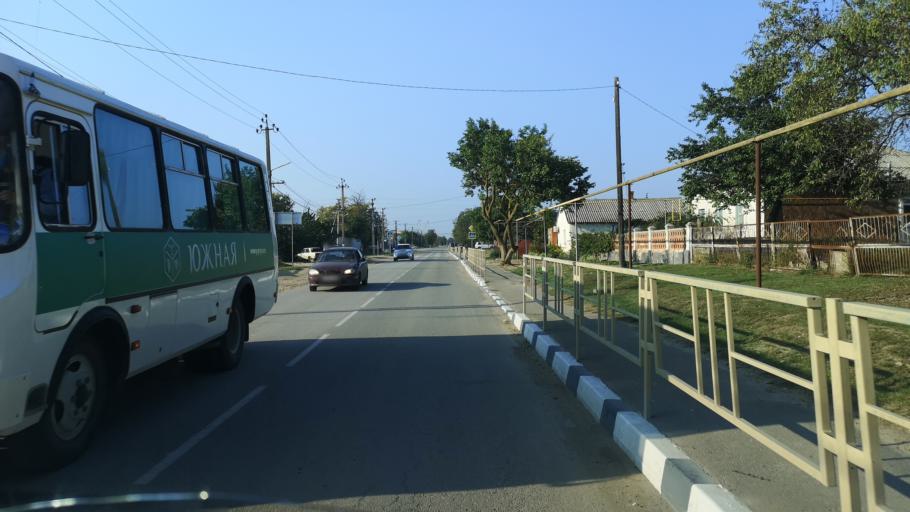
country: RU
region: Krasnodarskiy
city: Taman'
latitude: 45.2108
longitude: 36.6984
